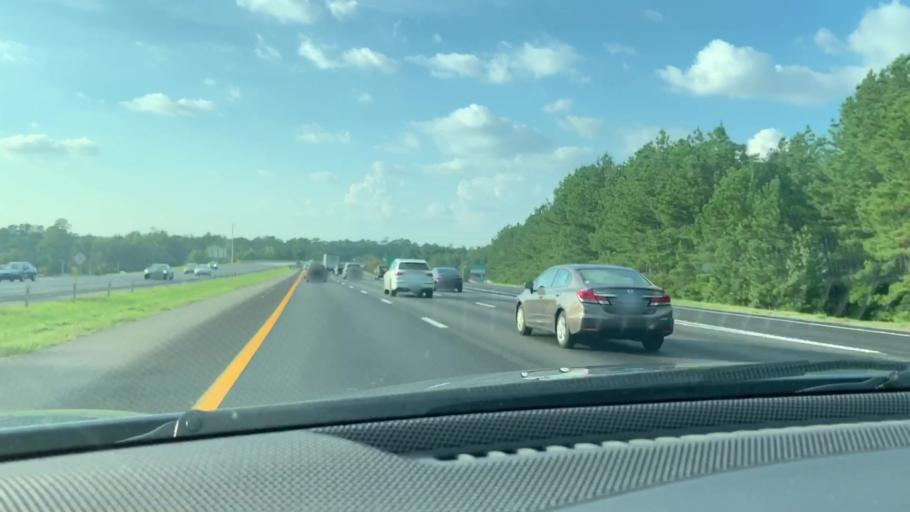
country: US
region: South Carolina
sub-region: Richland County
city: Forest Acres
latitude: 33.9929
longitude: -80.9559
